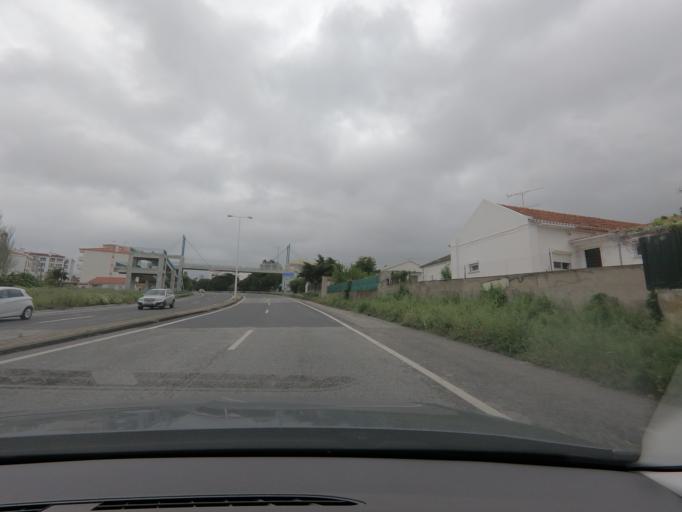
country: PT
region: Lisbon
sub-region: Cascais
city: Sao Domingos de Rana
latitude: 38.7030
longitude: -9.3339
